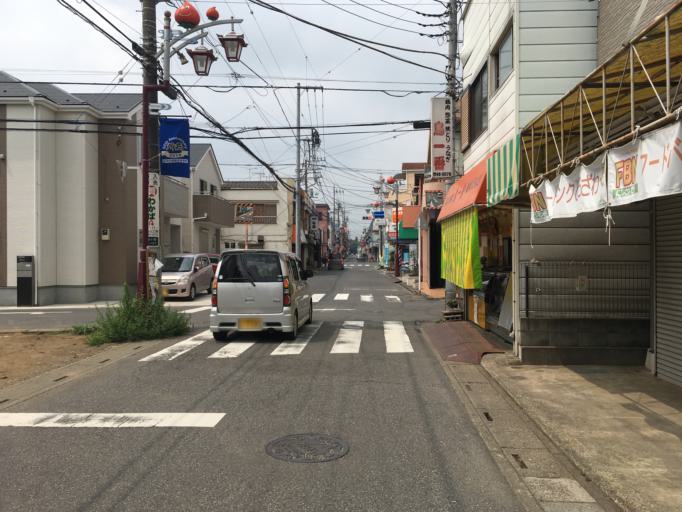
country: JP
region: Saitama
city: Sayama
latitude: 35.8066
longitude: 139.4093
